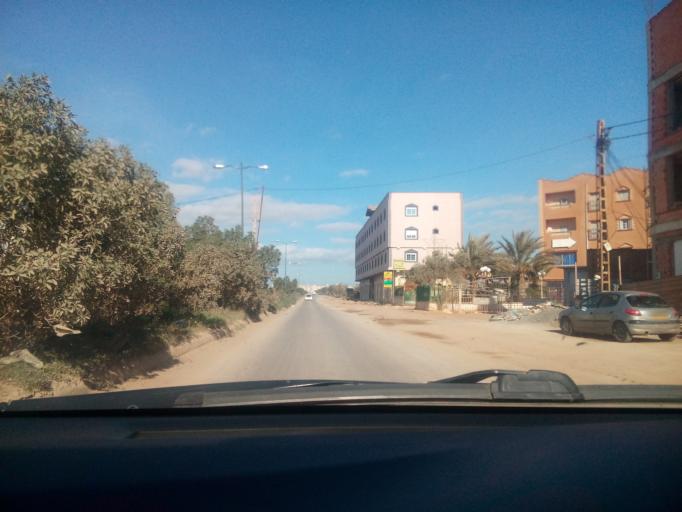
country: DZ
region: Oran
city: Sidi ech Chahmi
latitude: 35.6552
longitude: -0.5677
